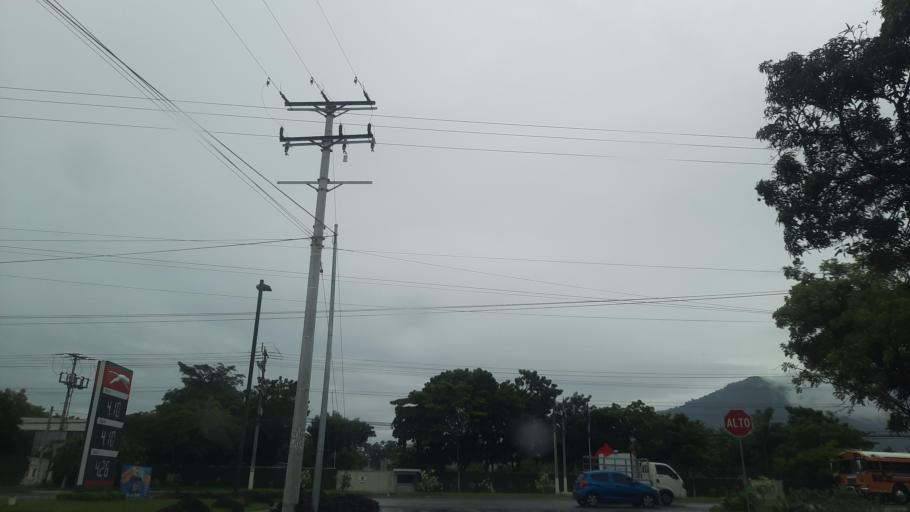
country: SV
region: La Libertad
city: Ciudad Arce
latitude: 13.7655
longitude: -89.3701
